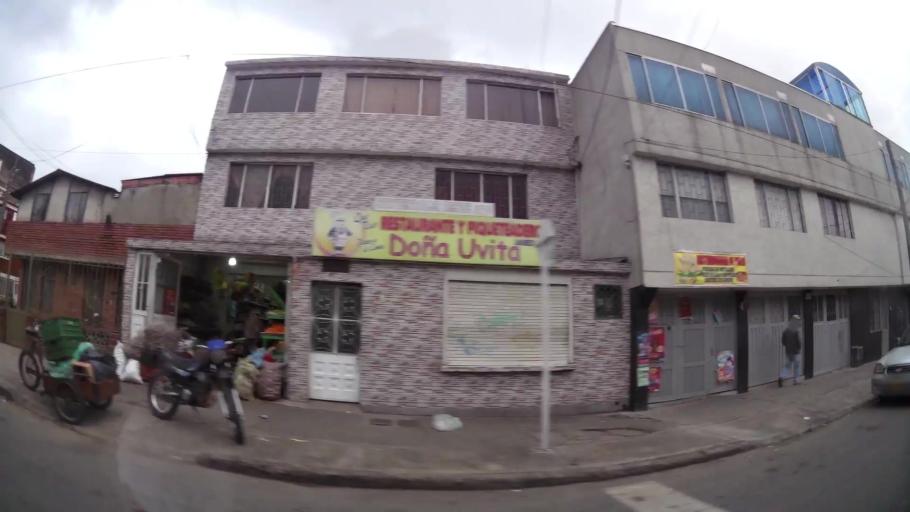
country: CO
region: Bogota D.C.
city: Bogota
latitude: 4.6884
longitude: -74.1047
